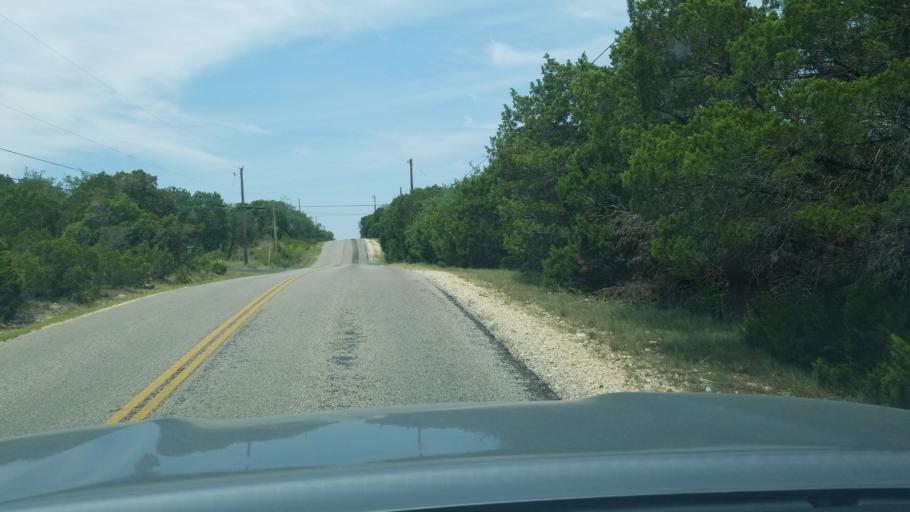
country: US
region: Texas
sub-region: Comal County
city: Bulverde
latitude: 29.7758
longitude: -98.4361
